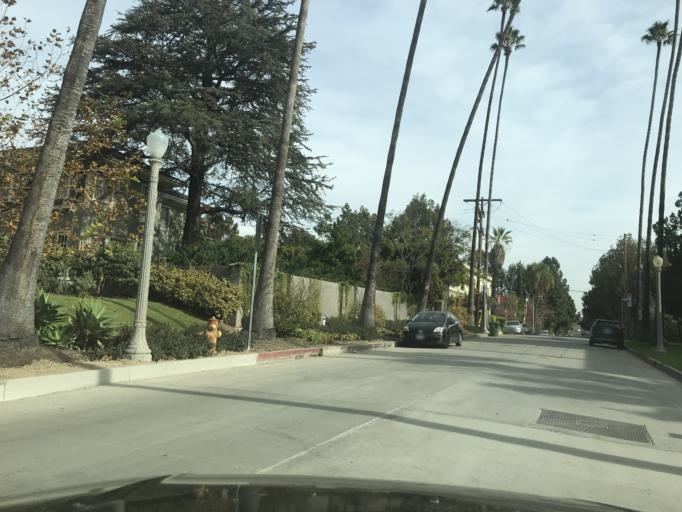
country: US
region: California
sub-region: Los Angeles County
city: Hollywood
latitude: 34.0653
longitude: -118.3185
